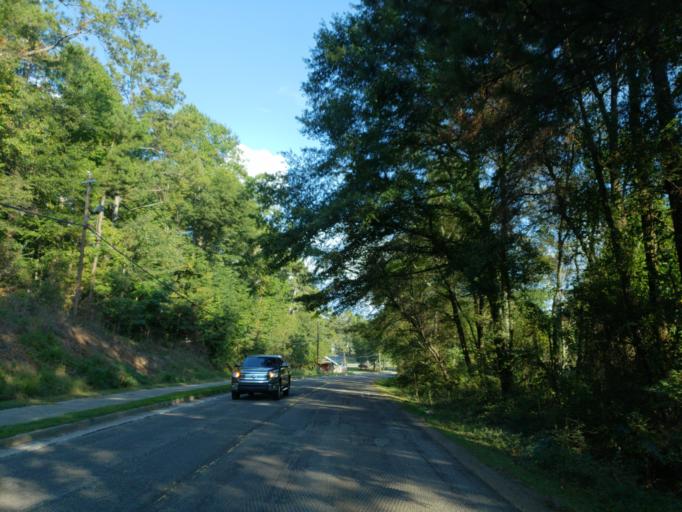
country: US
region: Georgia
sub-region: Cobb County
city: Powder Springs
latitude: 33.8624
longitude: -84.6888
